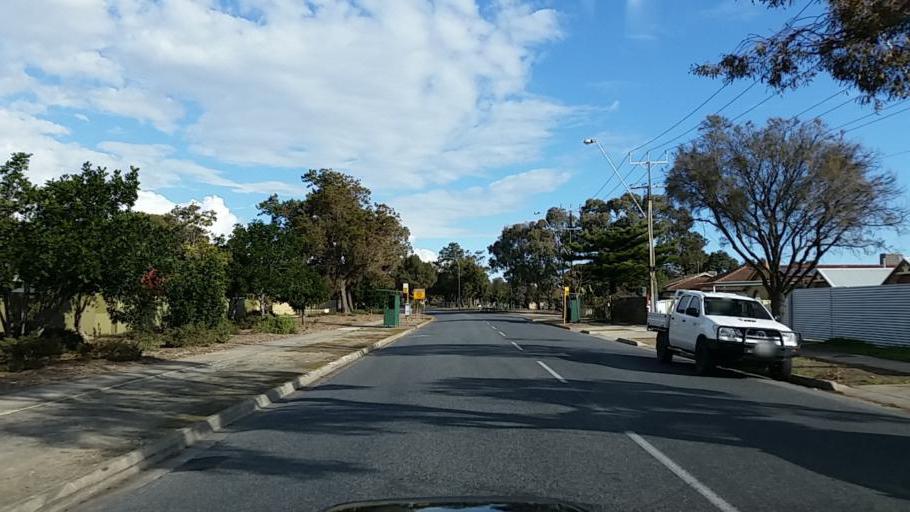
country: AU
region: South Australia
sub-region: Charles Sturt
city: West Lakes Shore
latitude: -34.8528
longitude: 138.4930
